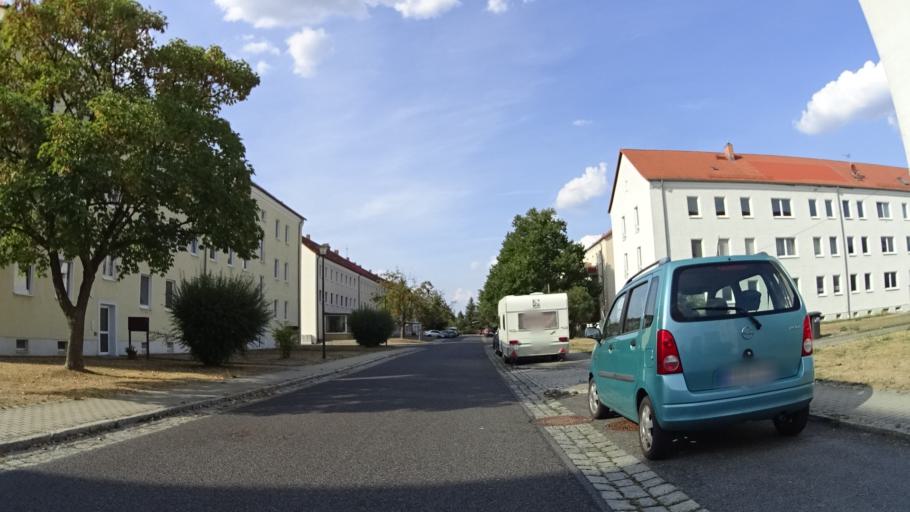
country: DE
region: Saxony
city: Ostritz
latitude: 51.0682
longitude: 14.9628
